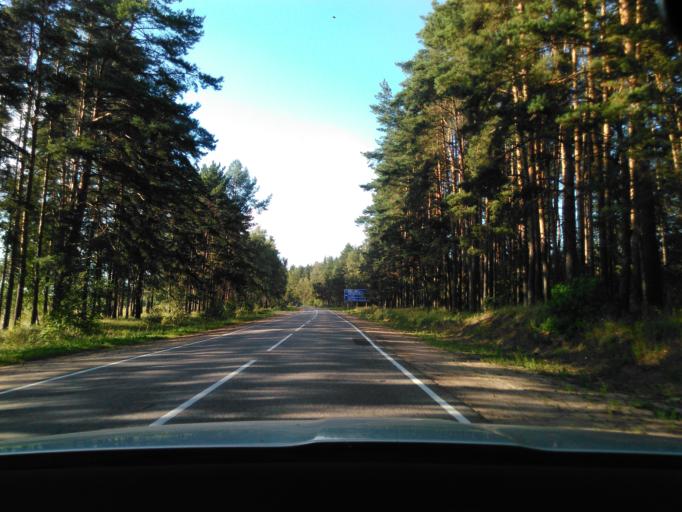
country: RU
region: Tverskaya
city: Zavidovo
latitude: 56.5900
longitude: 36.5413
